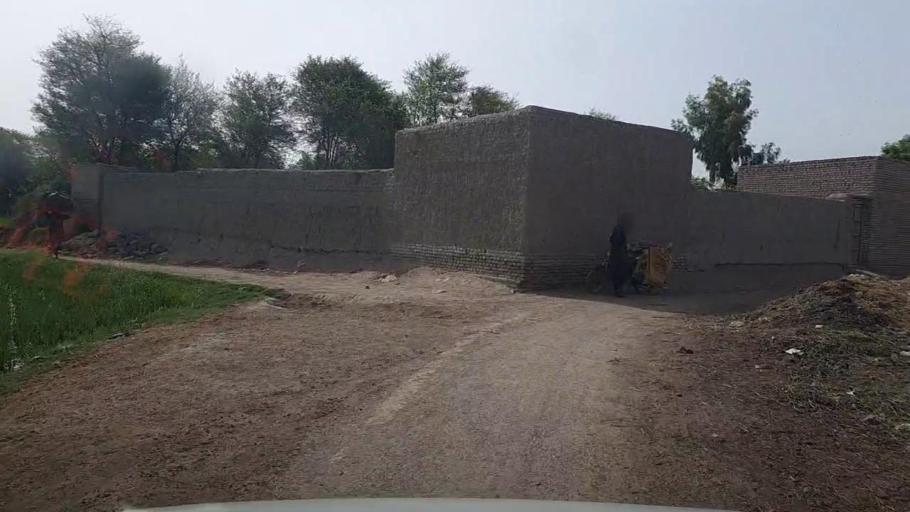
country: PK
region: Sindh
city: Sita Road
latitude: 27.0987
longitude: 67.8251
